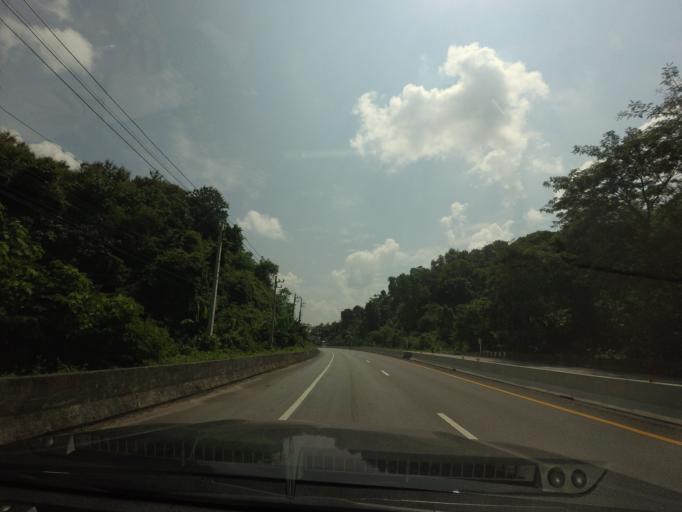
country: TH
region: Uttaradit
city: Lap Lae
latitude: 17.7781
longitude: 100.1237
